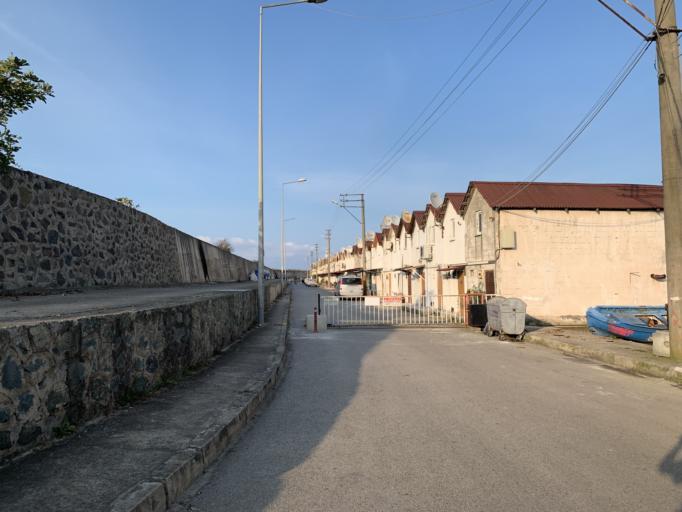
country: TR
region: Trabzon
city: Trabzon
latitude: 41.0029
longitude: 39.7604
